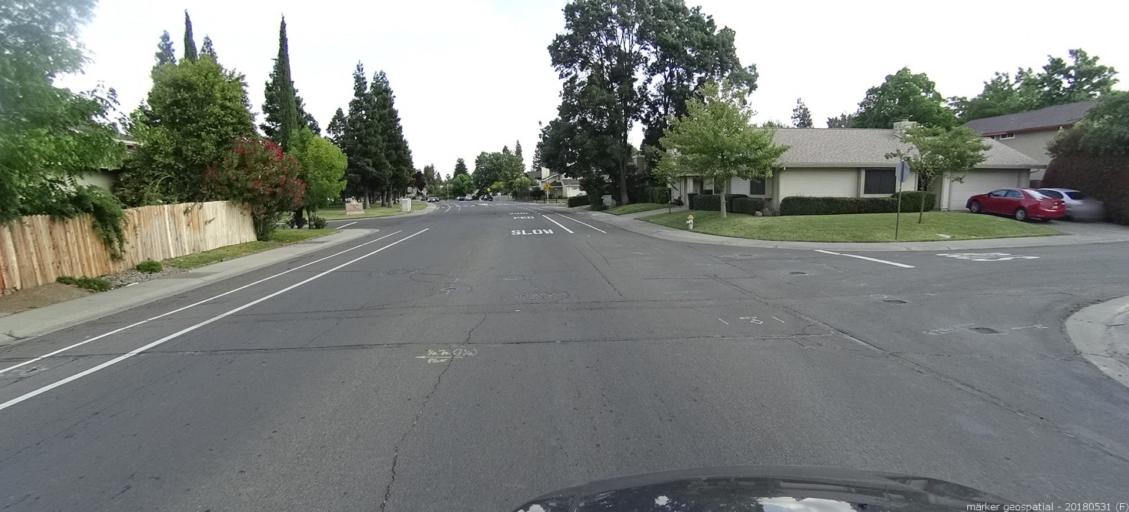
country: US
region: California
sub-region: Sacramento County
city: Sacramento
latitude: 38.6287
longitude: -121.4872
